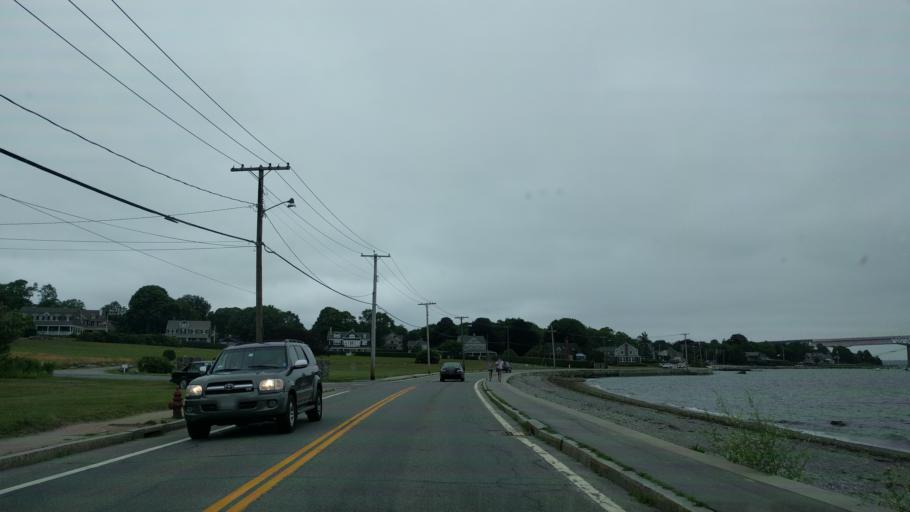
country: US
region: Rhode Island
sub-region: Newport County
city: Jamestown
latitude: 41.4978
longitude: -71.3669
